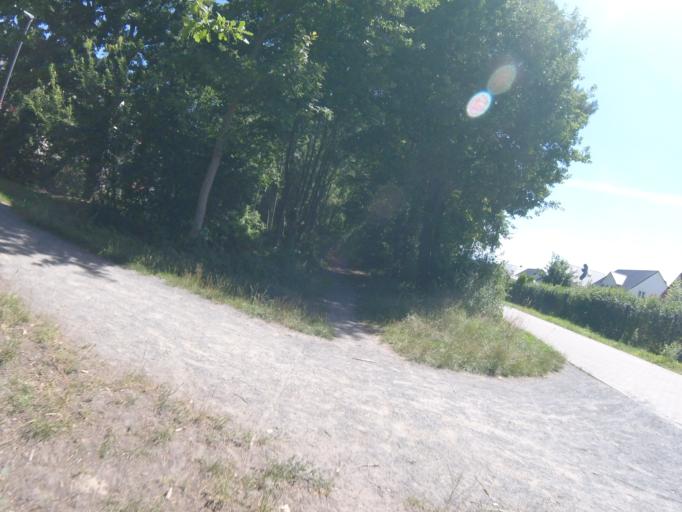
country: DE
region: Brandenburg
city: Konigs Wusterhausen
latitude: 52.2847
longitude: 13.6105
